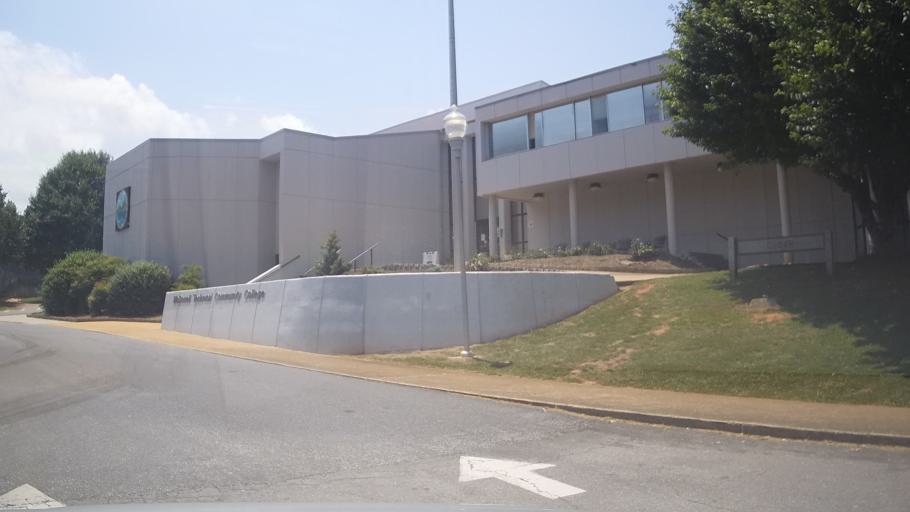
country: US
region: North Carolina
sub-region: McDowell County
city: Marion
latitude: 35.6564
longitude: -81.9616
